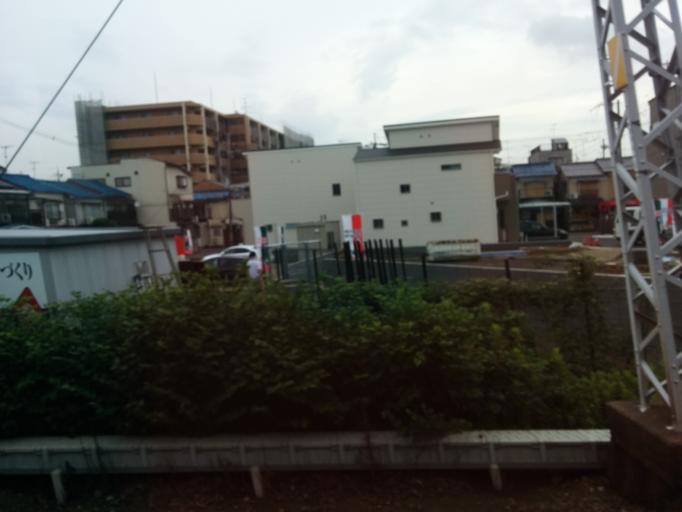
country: JP
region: Kyoto
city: Muko
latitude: 34.9562
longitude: 135.7043
